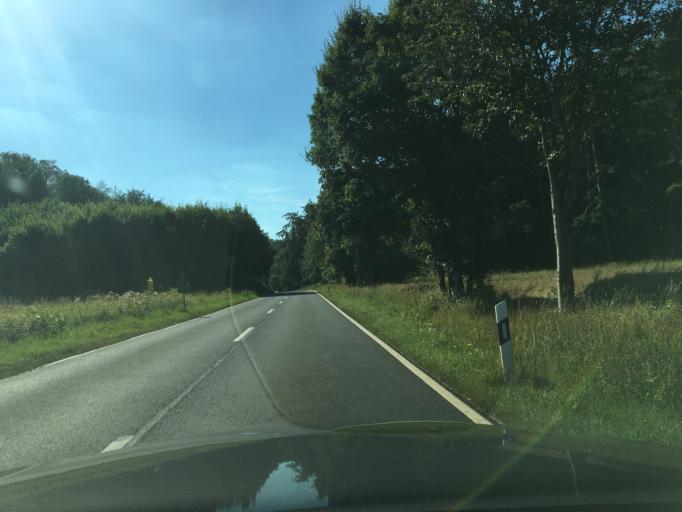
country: DE
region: Bavaria
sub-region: Upper Franconia
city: Hiltpoltstein
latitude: 49.6606
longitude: 11.3397
